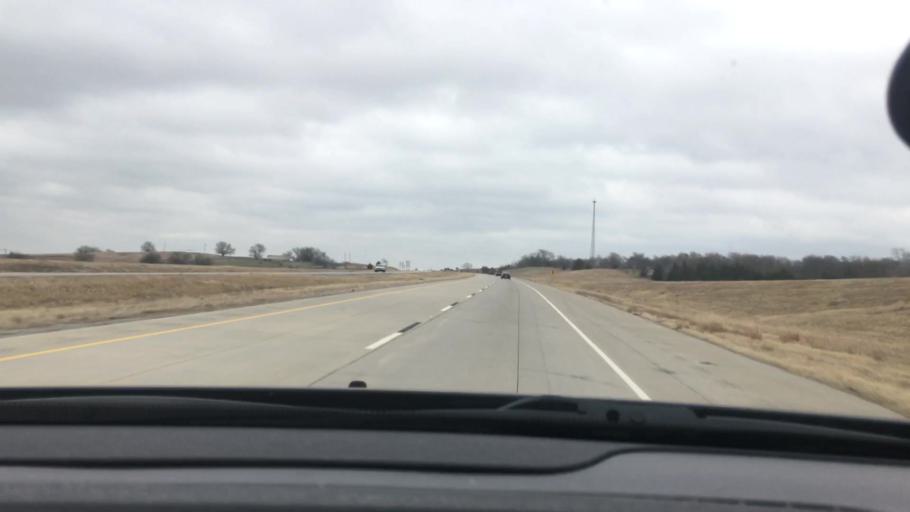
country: US
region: Oklahoma
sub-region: Bryan County
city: Durant
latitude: 34.1328
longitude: -96.2751
